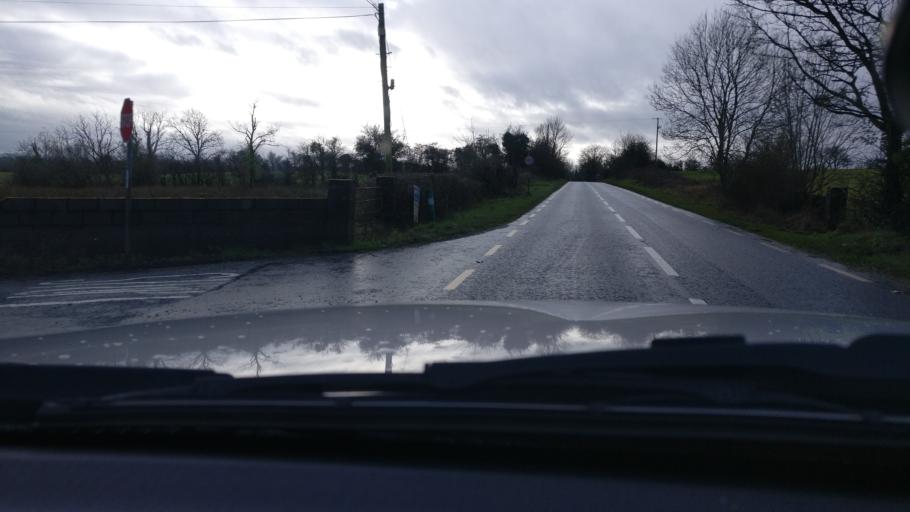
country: IE
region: Leinster
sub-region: An Iarmhi
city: Moate
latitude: 53.6164
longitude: -7.7040
